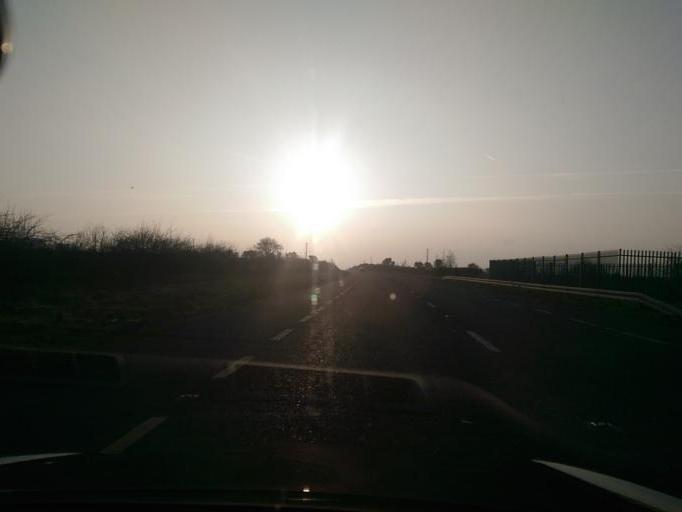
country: IE
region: Connaught
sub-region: County Galway
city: Loughrea
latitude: 53.2075
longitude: -8.5763
